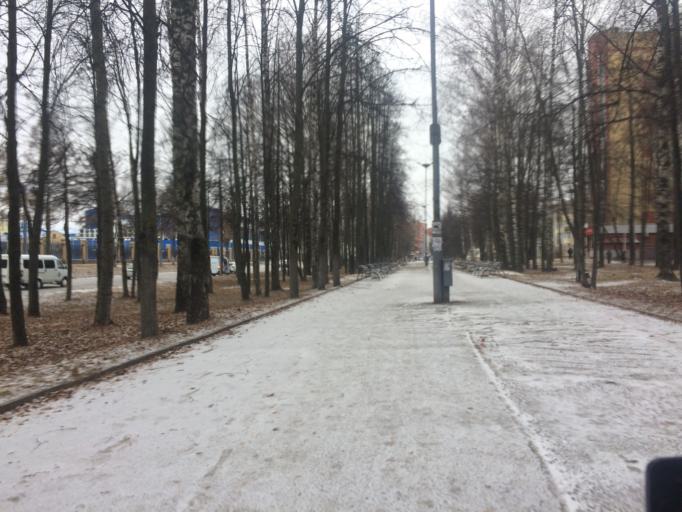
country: RU
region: Mariy-El
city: Yoshkar-Ola
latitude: 56.6432
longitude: 47.8729
